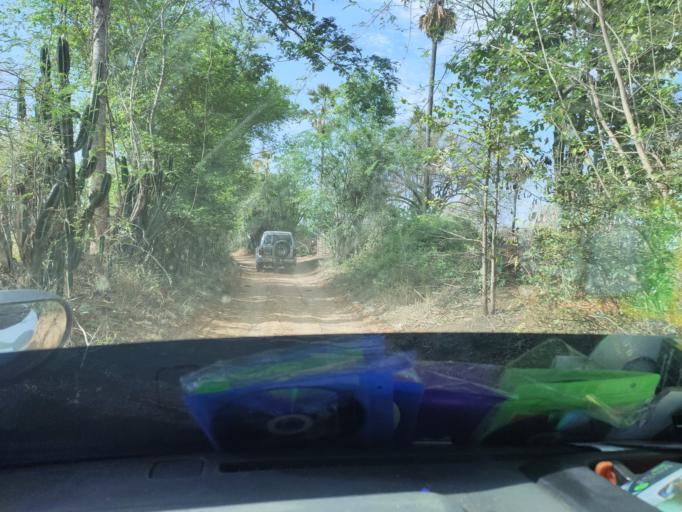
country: MM
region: Magway
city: Chauk
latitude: 20.9572
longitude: 94.9908
